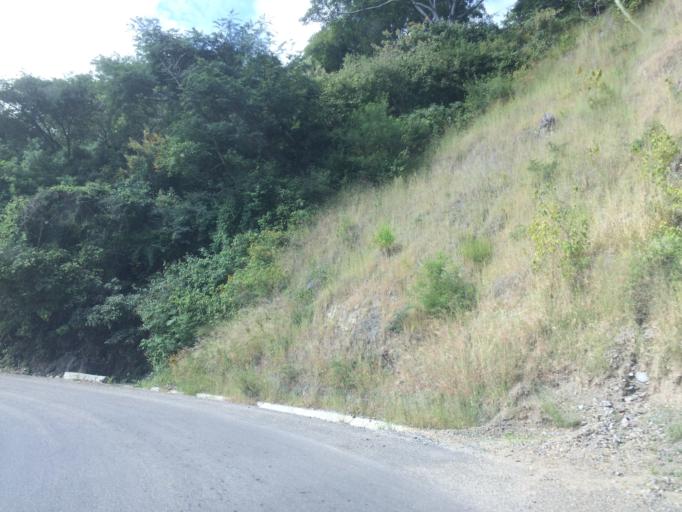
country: MX
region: Nayarit
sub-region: Ahuacatlan
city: Ahuacatlan
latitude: 21.0071
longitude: -104.4811
